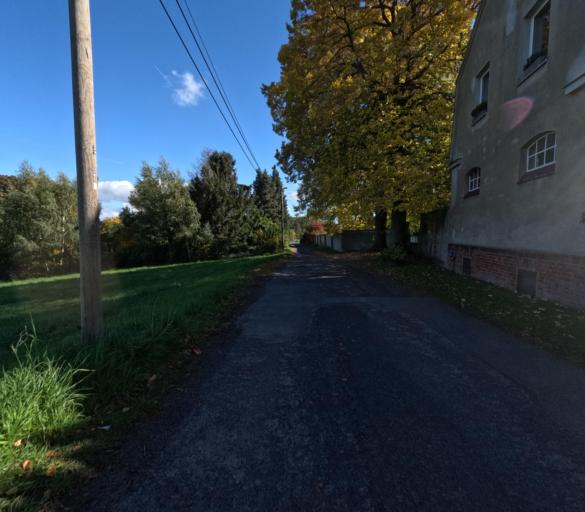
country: DE
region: Saxony
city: Radebeul
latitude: 51.1146
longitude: 13.6840
